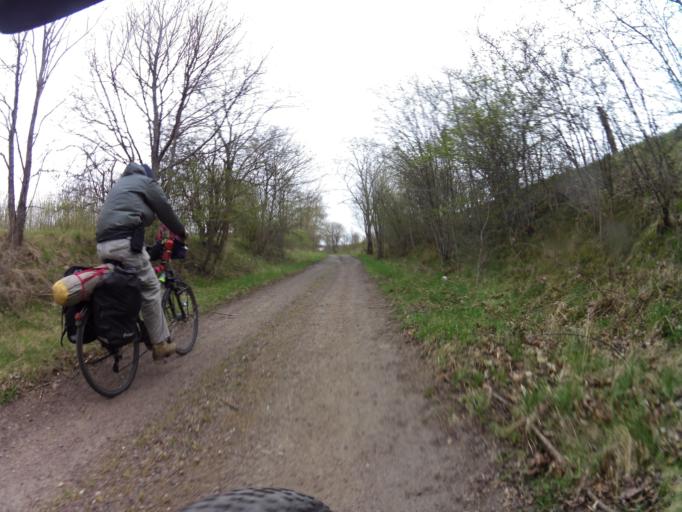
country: PL
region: West Pomeranian Voivodeship
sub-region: Powiat koszalinski
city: Bobolice
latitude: 53.9895
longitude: 16.6811
